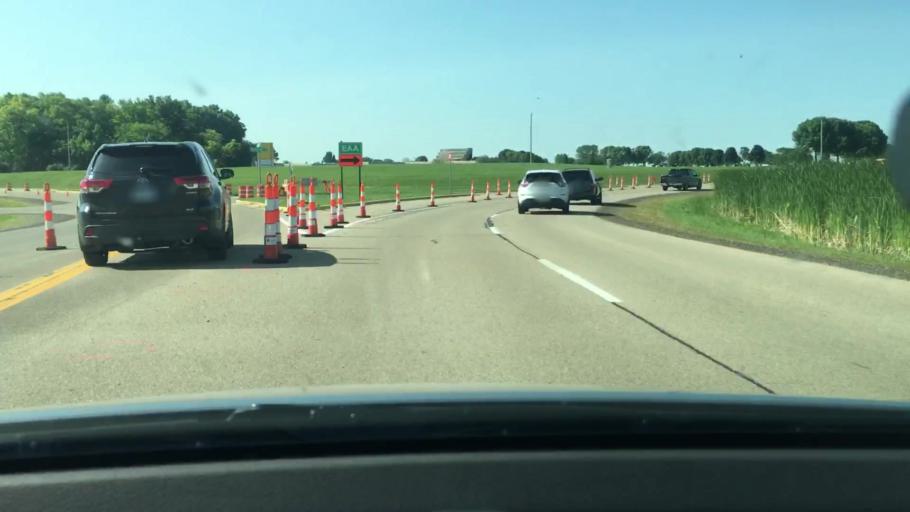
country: US
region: Wisconsin
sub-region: Winnebago County
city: Oshkosh
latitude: 43.9904
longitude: -88.5778
